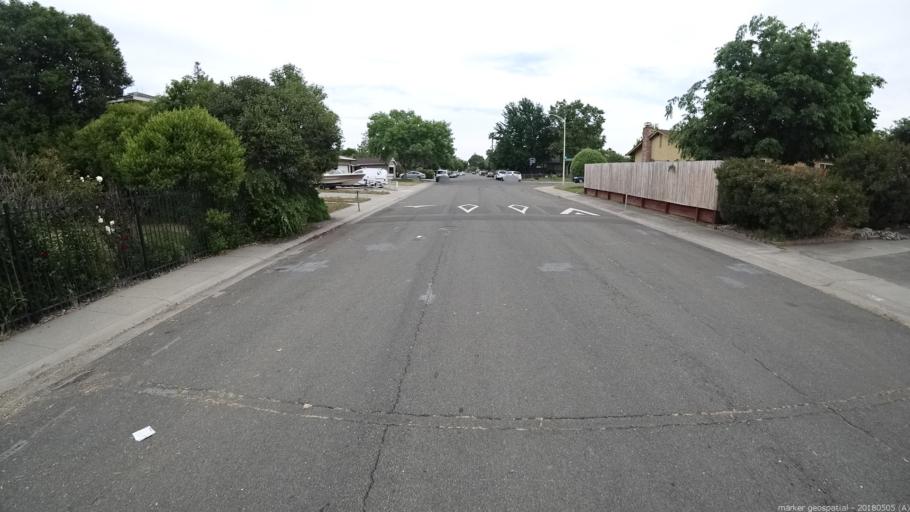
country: US
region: California
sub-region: Sacramento County
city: Rio Linda
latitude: 38.6508
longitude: -121.4681
